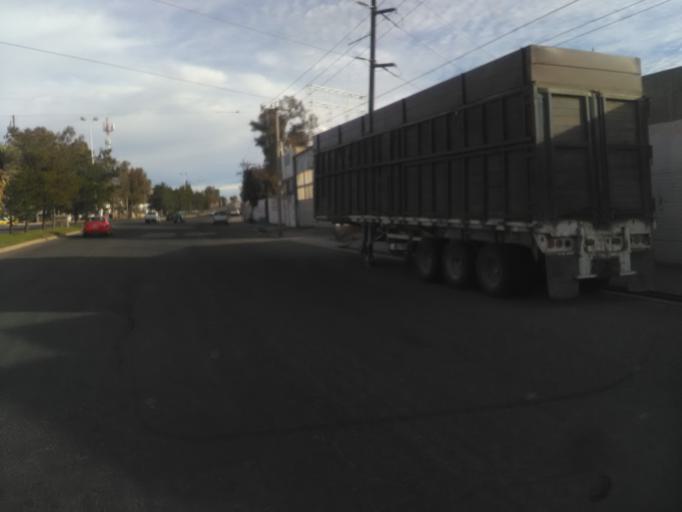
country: MX
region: Durango
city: Victoria de Durango
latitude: 24.0463
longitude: -104.6583
